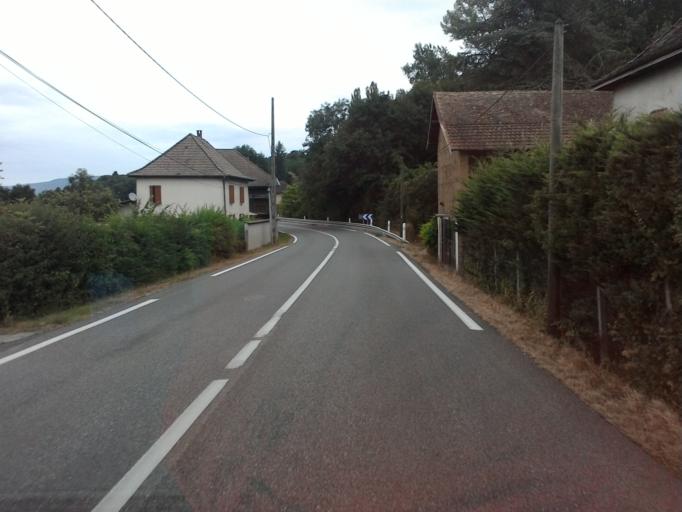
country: FR
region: Rhone-Alpes
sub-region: Departement de l'Isere
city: Corbelin
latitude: 45.6142
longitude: 5.5395
